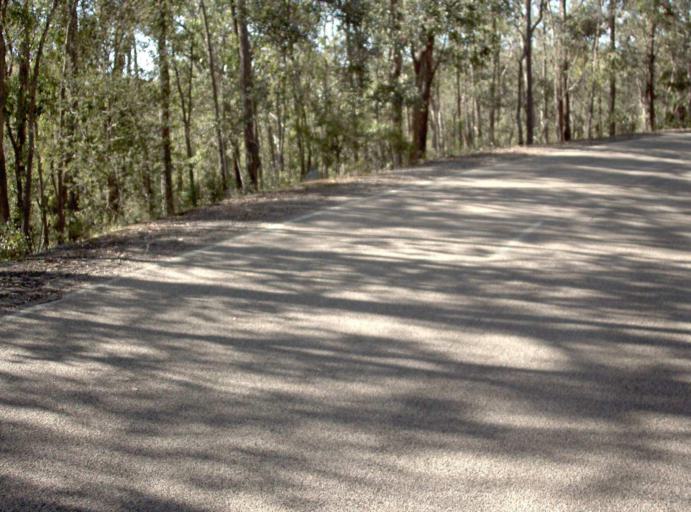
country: AU
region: Victoria
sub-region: East Gippsland
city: Lakes Entrance
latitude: -37.5550
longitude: 148.5621
